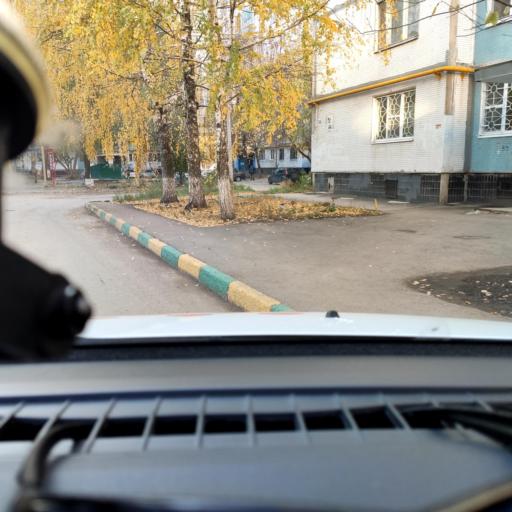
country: RU
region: Samara
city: Samara
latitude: 53.1894
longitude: 50.1454
